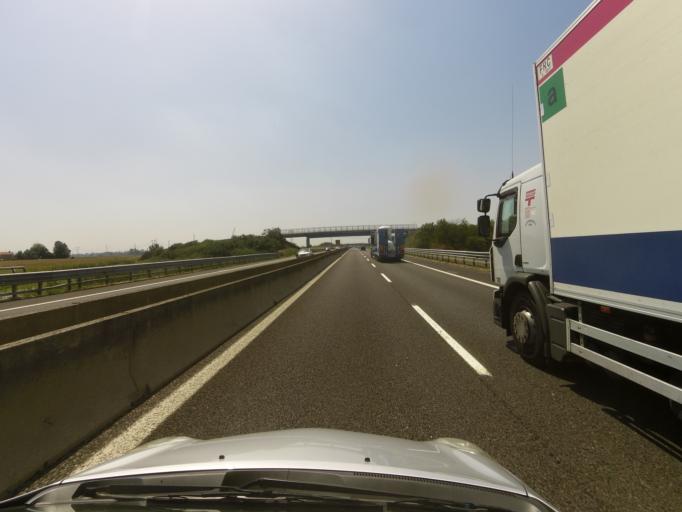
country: IT
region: Veneto
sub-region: Provincia di Rovigo
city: Occhiobello
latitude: 44.8919
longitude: 11.5701
